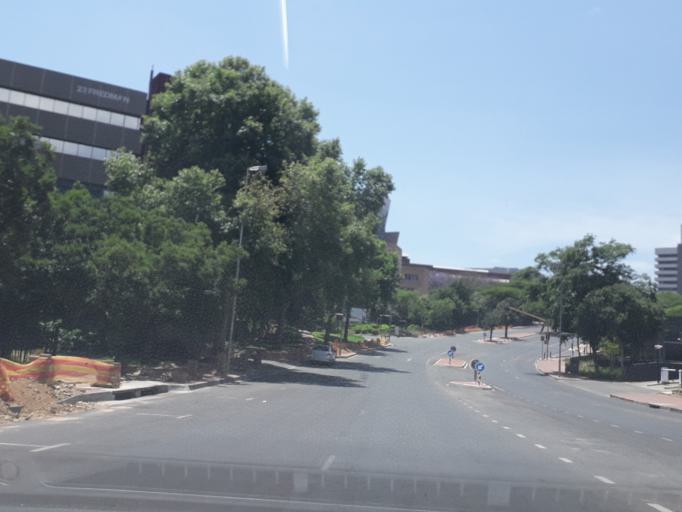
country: ZA
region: Gauteng
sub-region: City of Johannesburg Metropolitan Municipality
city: Johannesburg
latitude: -26.1045
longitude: 28.0506
